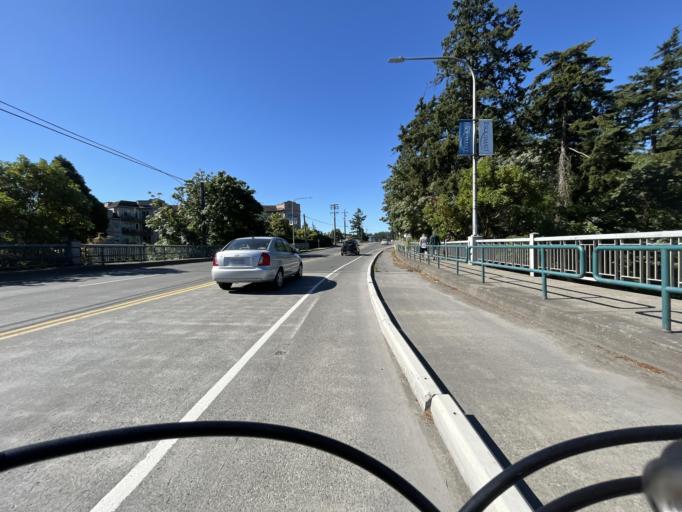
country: CA
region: British Columbia
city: Victoria
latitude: 48.4463
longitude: -123.4005
